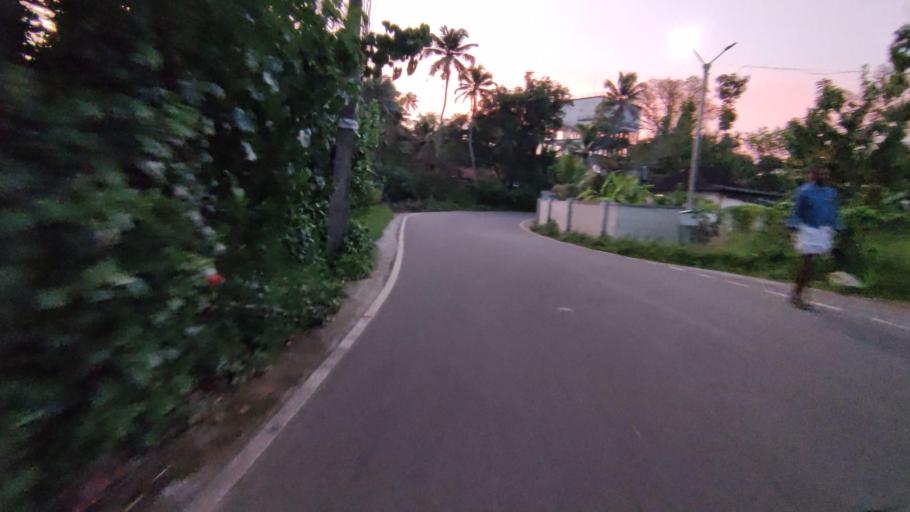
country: IN
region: Kerala
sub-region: Kottayam
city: Kottayam
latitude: 9.5885
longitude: 76.4371
